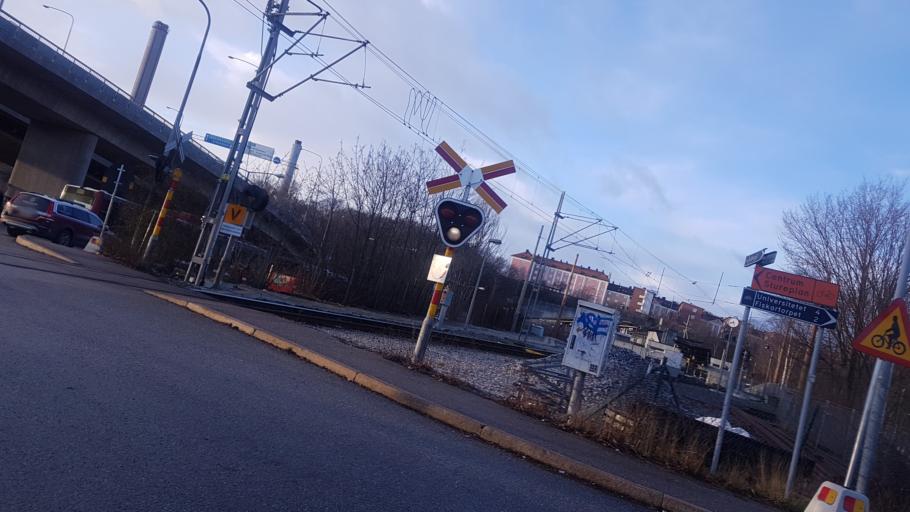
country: SE
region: Stockholm
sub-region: Stockholms Kommun
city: OEstermalm
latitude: 59.3586
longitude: 18.1051
